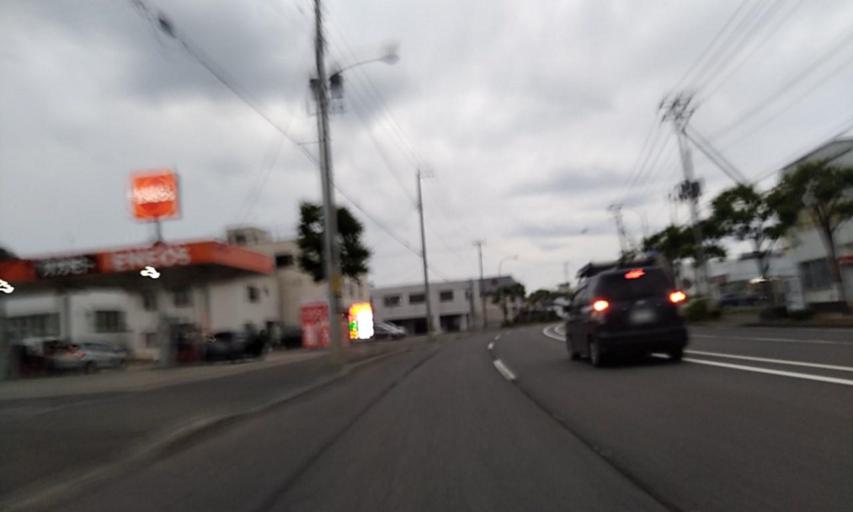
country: JP
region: Hokkaido
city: Abashiri
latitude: 44.0197
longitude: 144.2480
